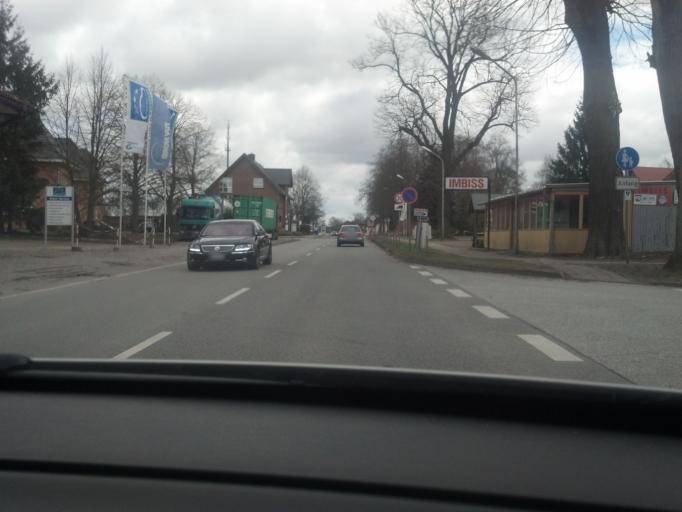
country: DE
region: Mecklenburg-Vorpommern
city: Rechlin
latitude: 53.2736
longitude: 12.8195
